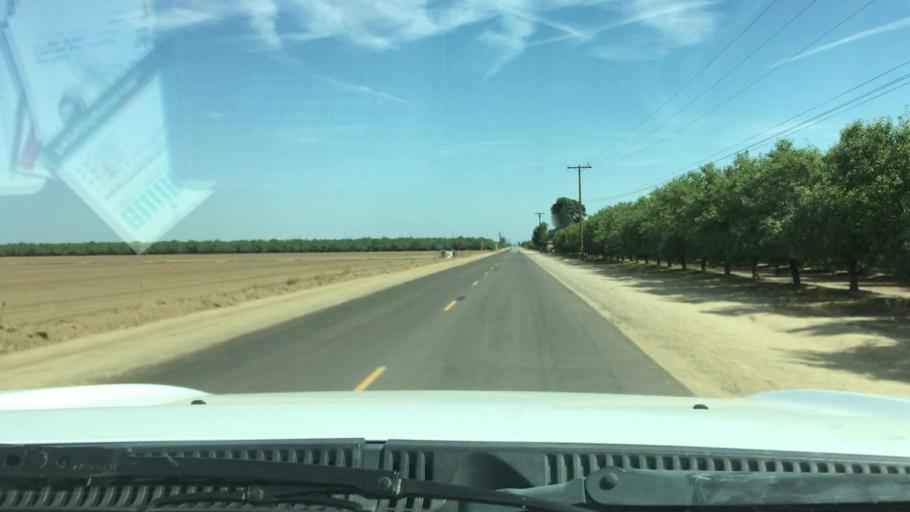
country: US
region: California
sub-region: Kern County
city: Wasco
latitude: 35.5165
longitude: -119.3499
